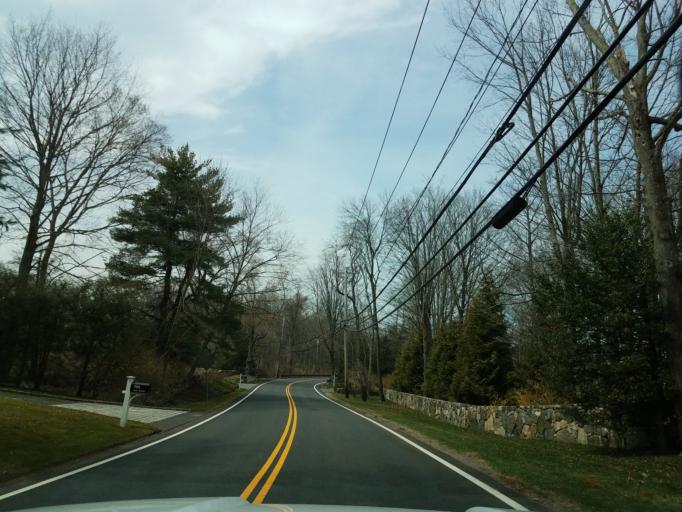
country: US
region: Connecticut
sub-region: Fairfield County
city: Glenville
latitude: 41.0817
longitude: -73.6445
